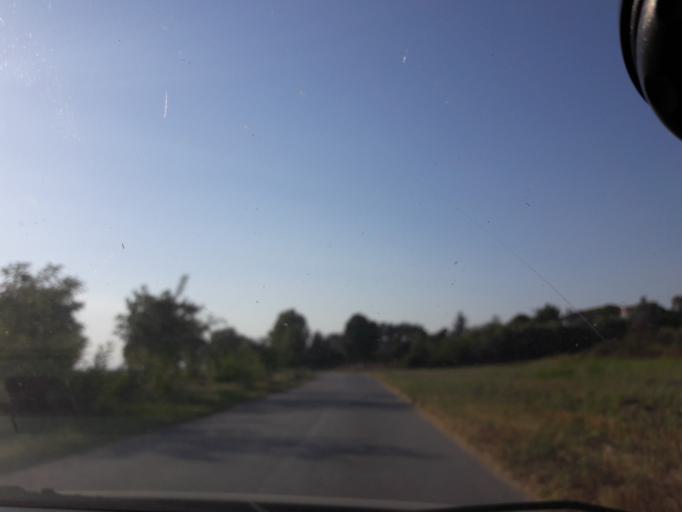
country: GR
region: Central Macedonia
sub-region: Nomos Chalkidikis
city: Nea Kallikrateia
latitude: 40.3348
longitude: 23.0224
